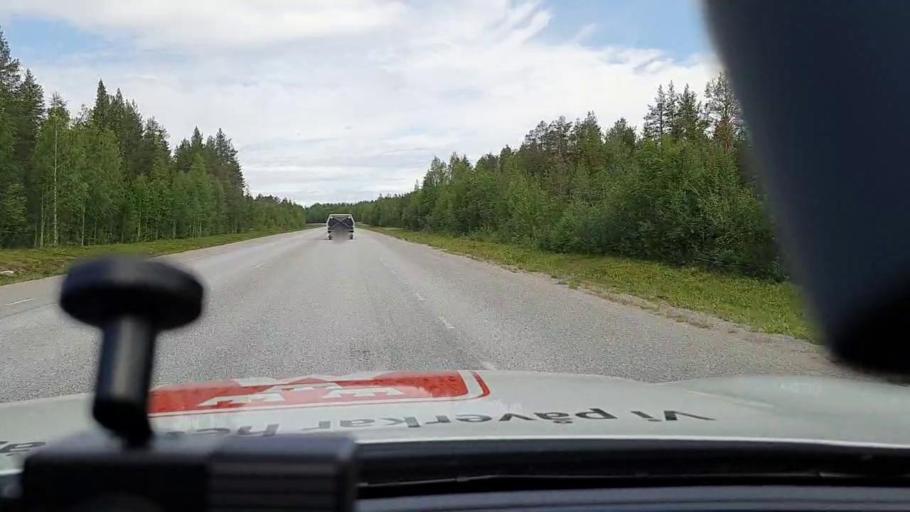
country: SE
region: Norrbotten
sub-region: Jokkmokks Kommun
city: Jokkmokk
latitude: 66.5054
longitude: 20.2503
